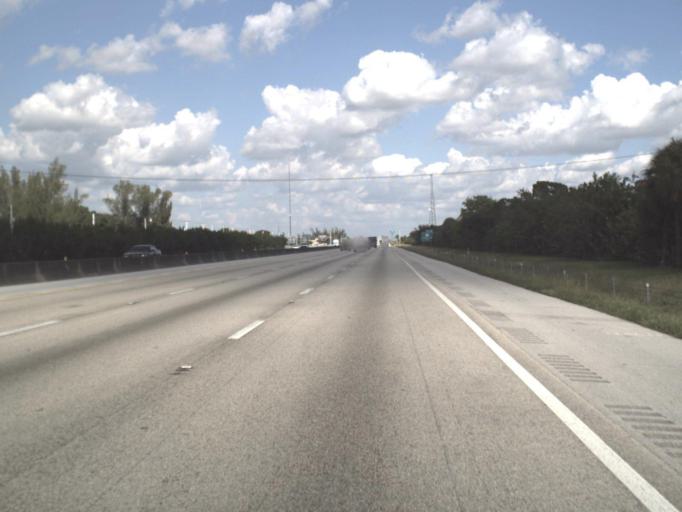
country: US
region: Florida
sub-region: Palm Beach County
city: Boca Pointe
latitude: 26.3562
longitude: -80.1705
